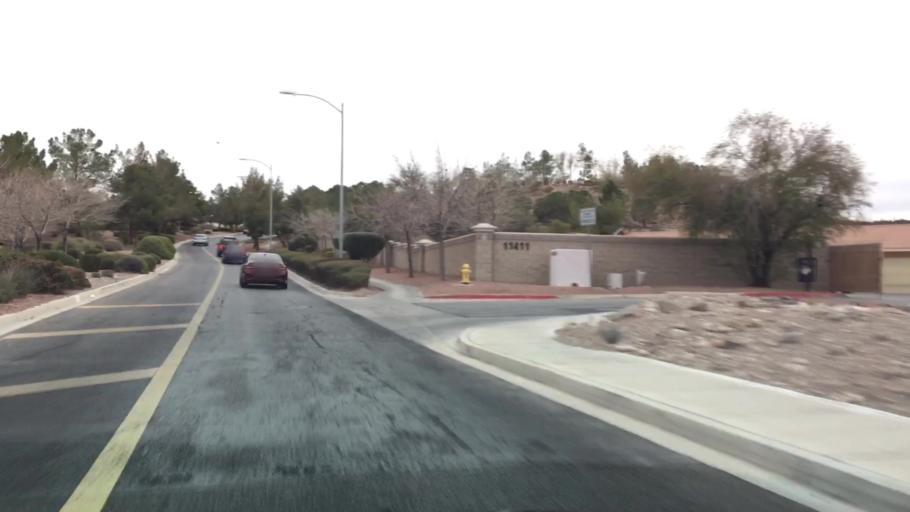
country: US
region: Nevada
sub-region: Clark County
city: Whitney
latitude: 35.9840
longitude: -115.1012
